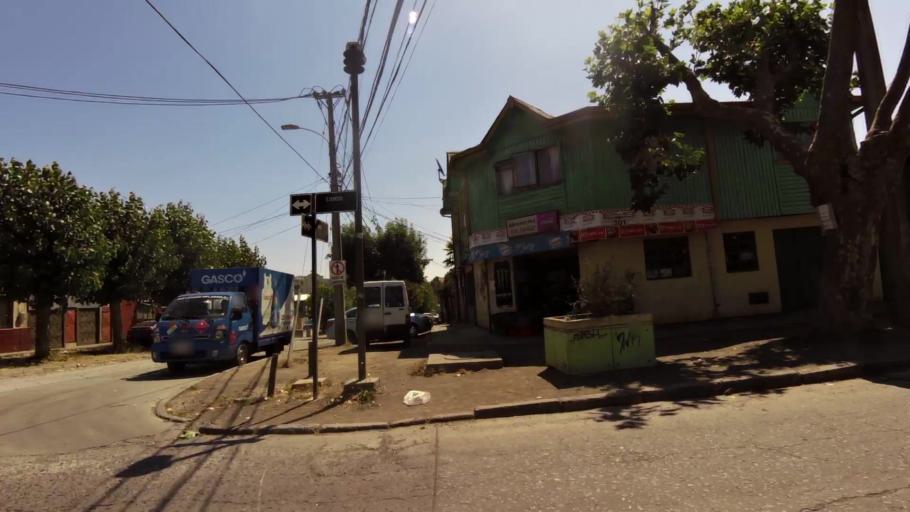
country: CL
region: Biobio
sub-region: Provincia de Concepcion
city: Concepcion
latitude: -36.8171
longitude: -73.0623
